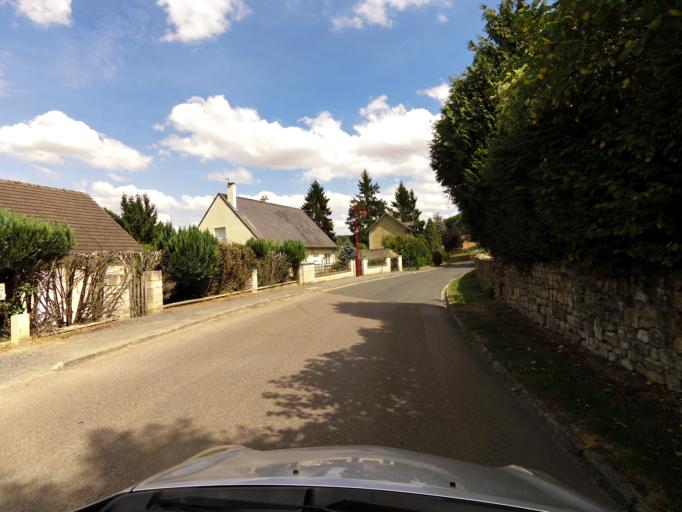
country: FR
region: Picardie
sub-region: Departement de l'Aisne
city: Neuilly-Saint-Front
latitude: 49.2522
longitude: 3.2085
